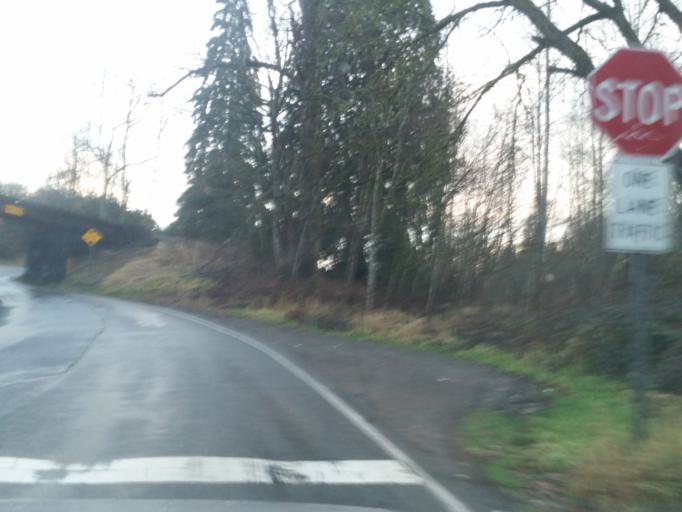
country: US
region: Washington
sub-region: Snohomish County
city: Cathcart
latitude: 47.8620
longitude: -122.0938
